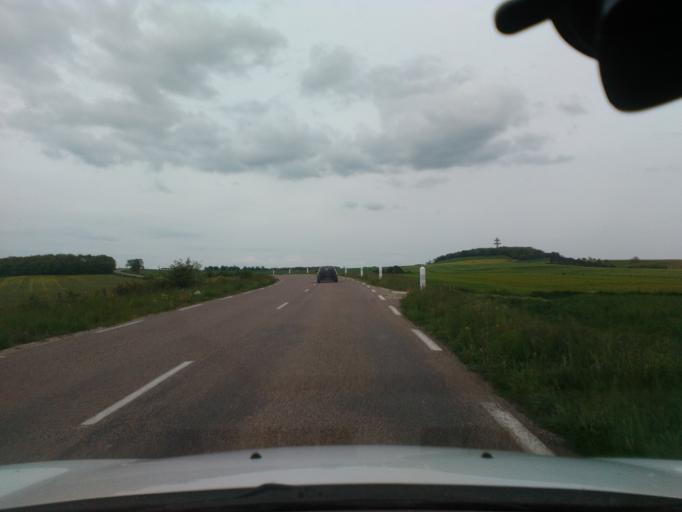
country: FR
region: Champagne-Ardenne
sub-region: Departement de la Haute-Marne
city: Lavilleneuve-au-Roi
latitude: 48.2239
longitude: 4.8564
